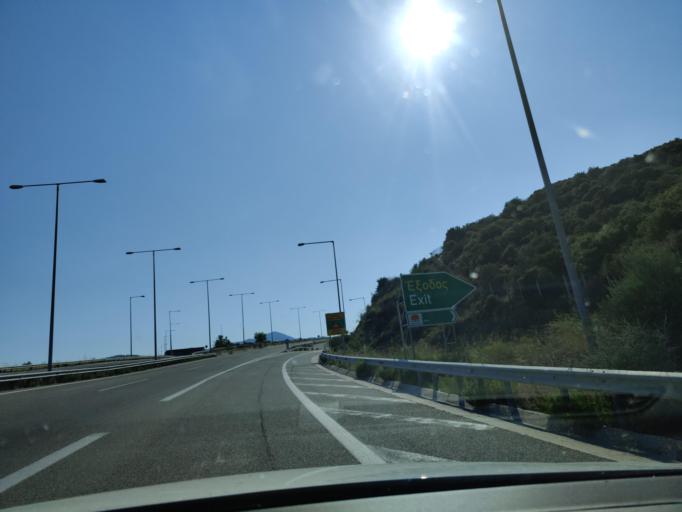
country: GR
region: East Macedonia and Thrace
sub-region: Nomos Kavalas
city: Nea Iraklitsa
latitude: 40.8762
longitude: 24.3006
